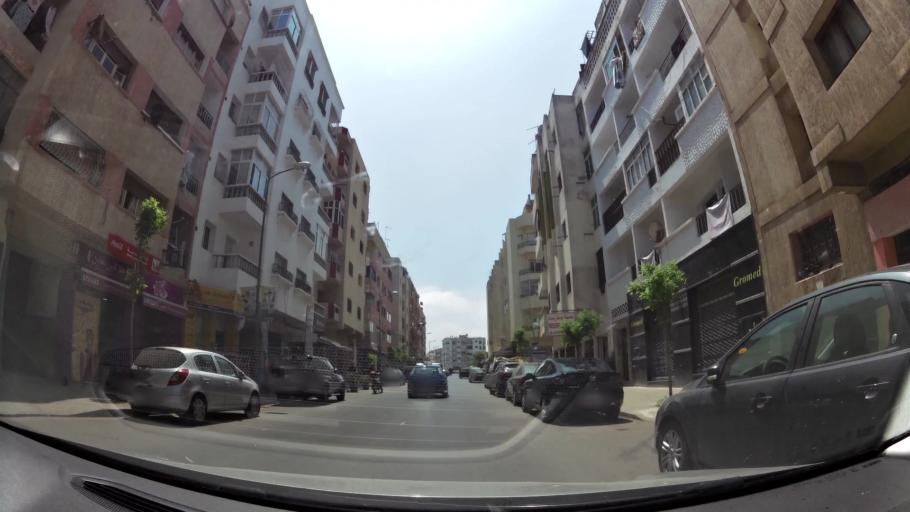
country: MA
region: Rabat-Sale-Zemmour-Zaer
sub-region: Rabat
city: Rabat
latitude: 34.0204
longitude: -6.8510
